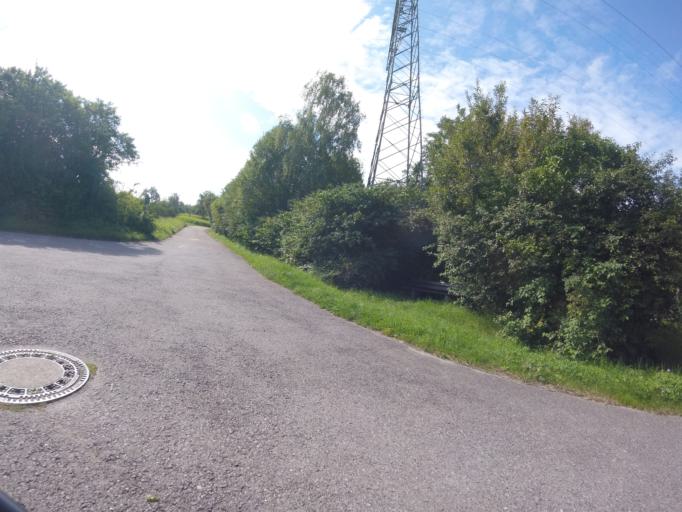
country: DE
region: Baden-Wuerttemberg
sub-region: Regierungsbezirk Stuttgart
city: Winnenden
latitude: 48.8655
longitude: 9.4051
